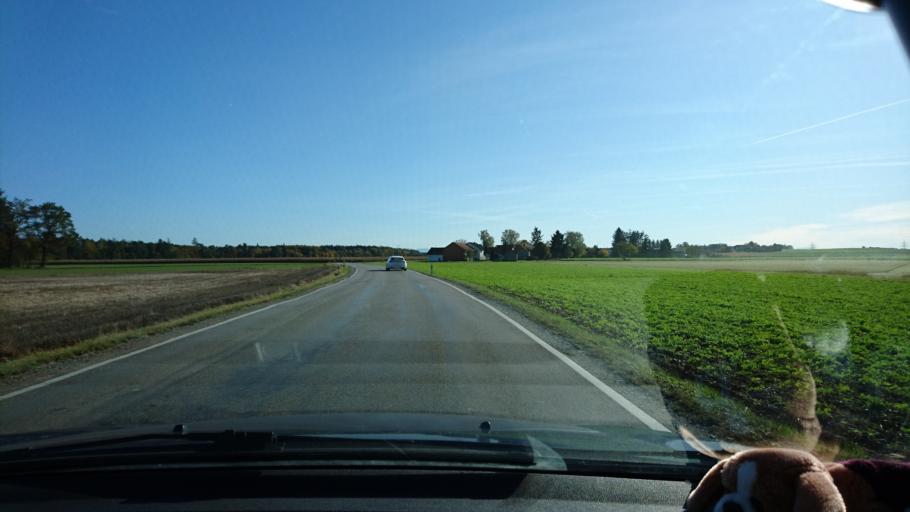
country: DE
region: Bavaria
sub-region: Upper Bavaria
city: Zorneding
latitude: 48.1170
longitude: 11.8337
